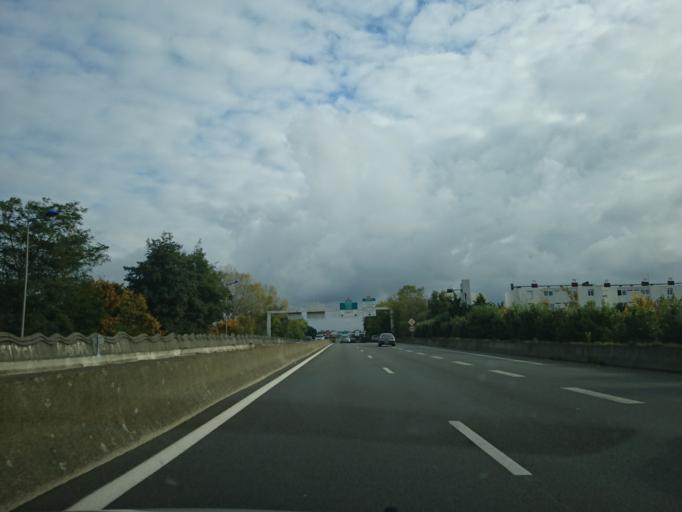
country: FR
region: Brittany
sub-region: Departement des Cotes-d'Armor
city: Langueux
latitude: 48.5106
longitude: -2.7402
